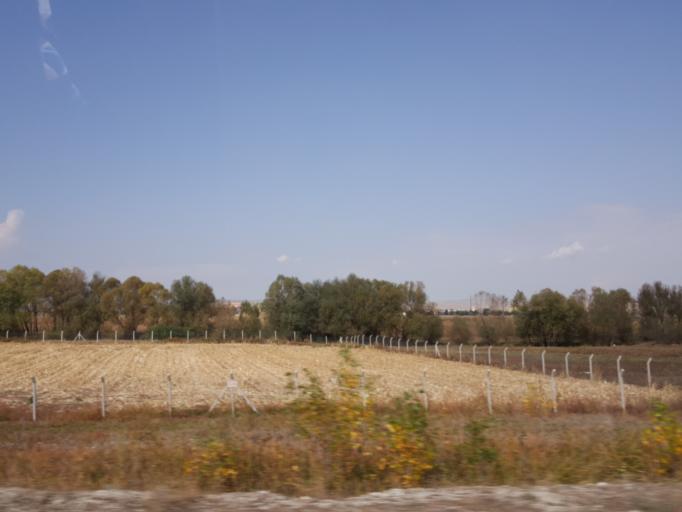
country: TR
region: Corum
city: Alaca
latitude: 40.1563
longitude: 34.8623
